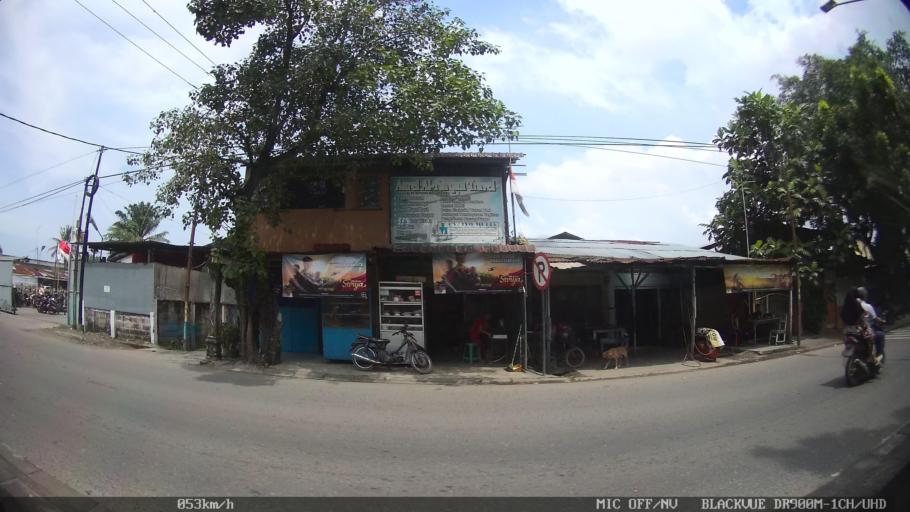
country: ID
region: North Sumatra
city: Medan
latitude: 3.6462
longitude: 98.6628
